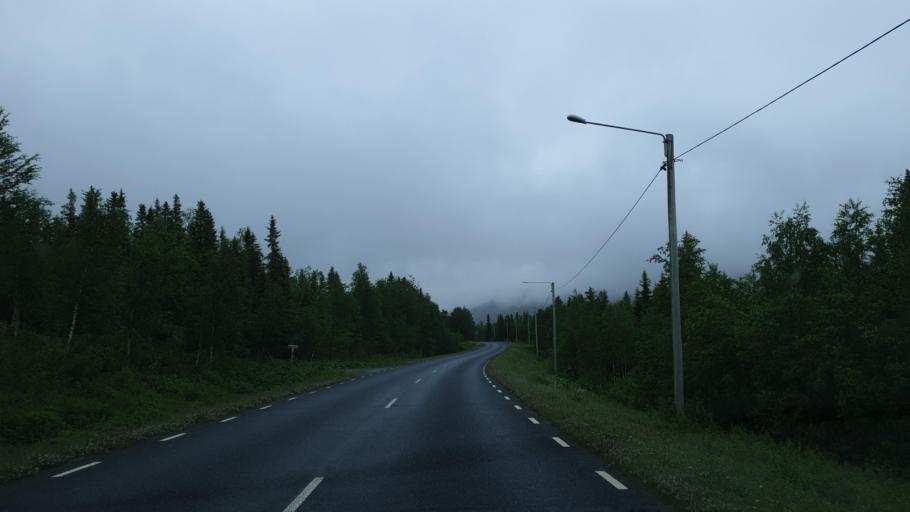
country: SE
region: Vaesterbotten
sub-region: Vilhelmina Kommun
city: Sjoberg
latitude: 65.2541
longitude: 15.5304
